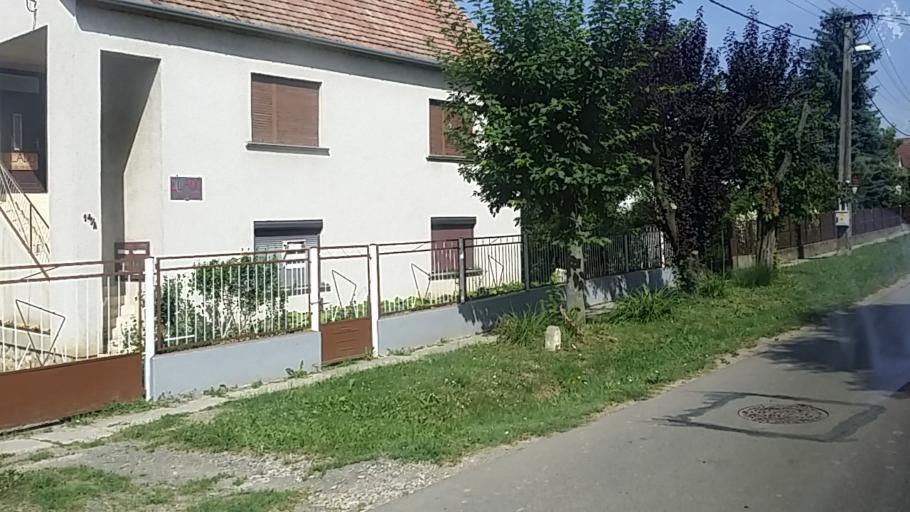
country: HU
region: Baranya
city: Villany
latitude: 45.8985
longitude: 18.3890
